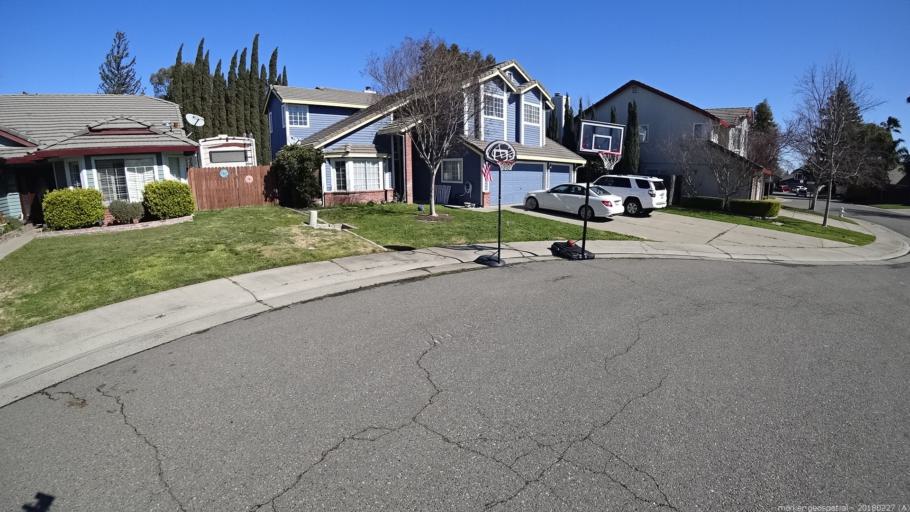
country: US
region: California
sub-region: Sacramento County
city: Antelope
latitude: 38.7153
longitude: -121.3513
